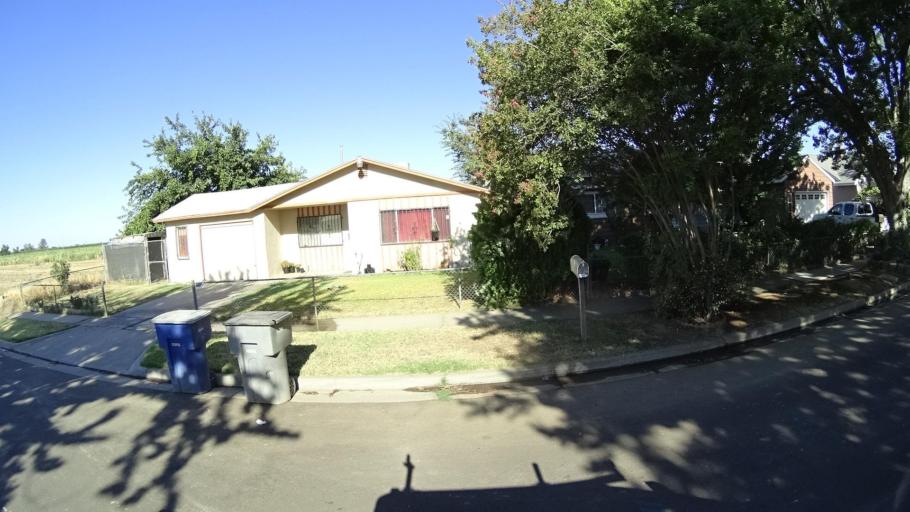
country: US
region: California
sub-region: Fresno County
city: West Park
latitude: 36.7033
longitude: -119.8017
